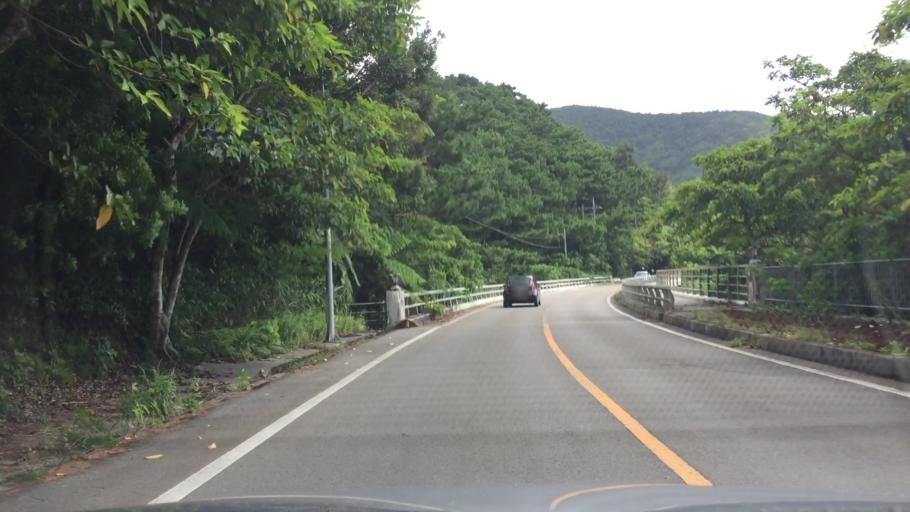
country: JP
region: Okinawa
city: Ishigaki
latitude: 24.4325
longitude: 124.2102
